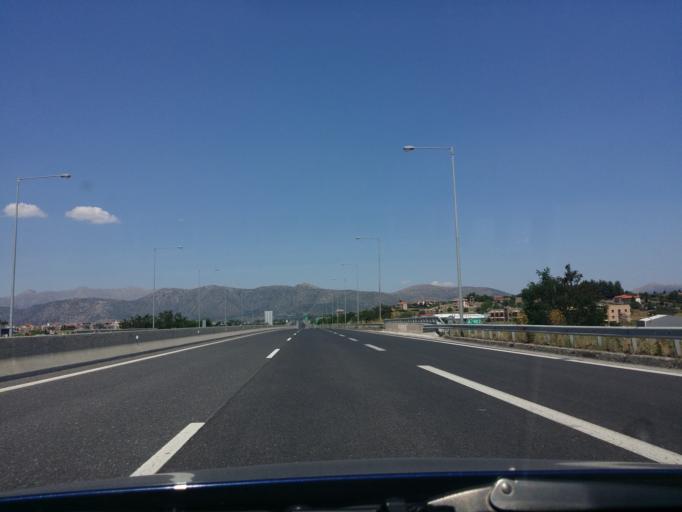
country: GR
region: Peloponnese
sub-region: Nomos Arkadias
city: Tripoli
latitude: 37.4949
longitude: 22.3814
